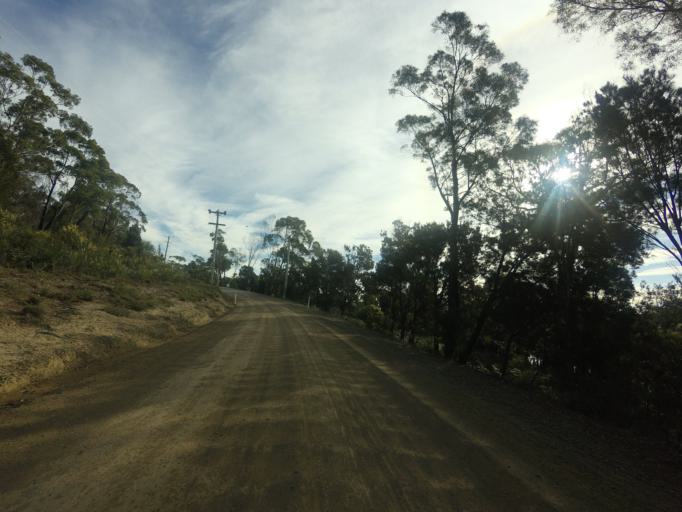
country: AU
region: Tasmania
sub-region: Sorell
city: Sorell
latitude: -42.9580
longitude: 147.8429
